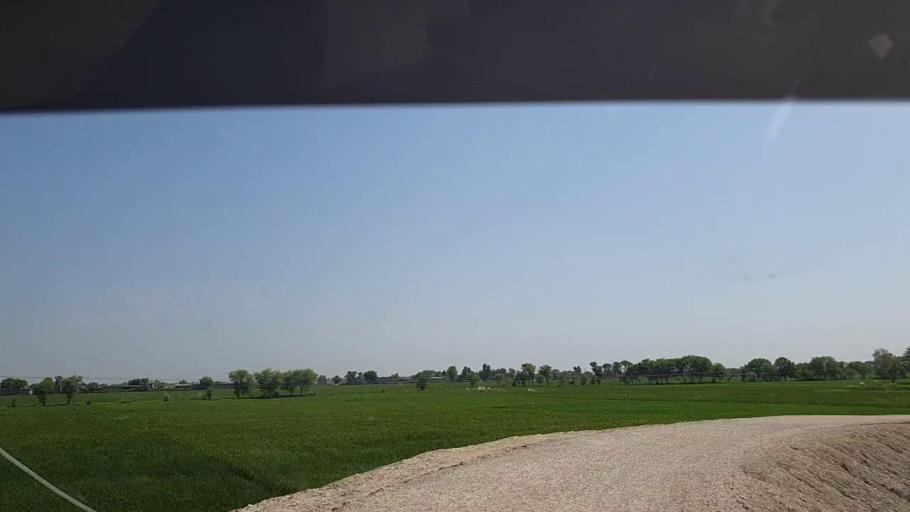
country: PK
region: Sindh
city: Kandhkot
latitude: 28.1889
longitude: 69.1630
